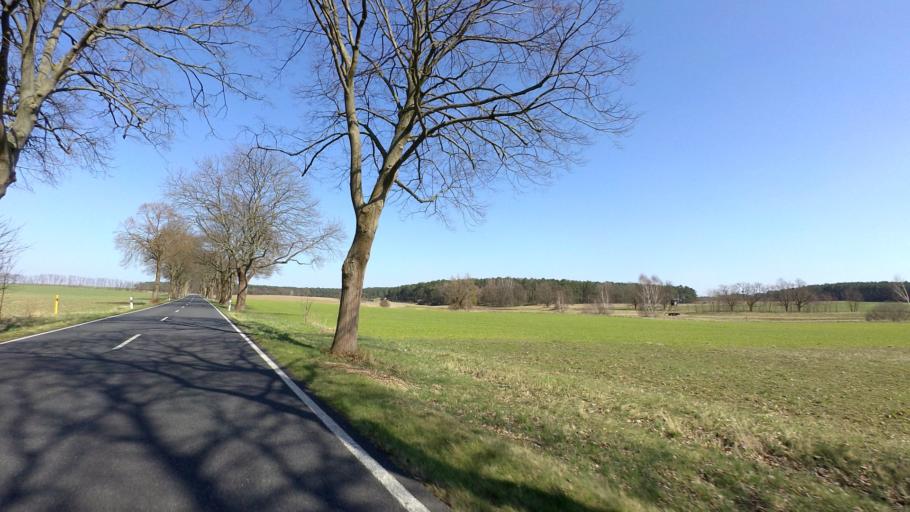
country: DE
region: Brandenburg
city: Sonnenberg
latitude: 52.9898
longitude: 13.0549
